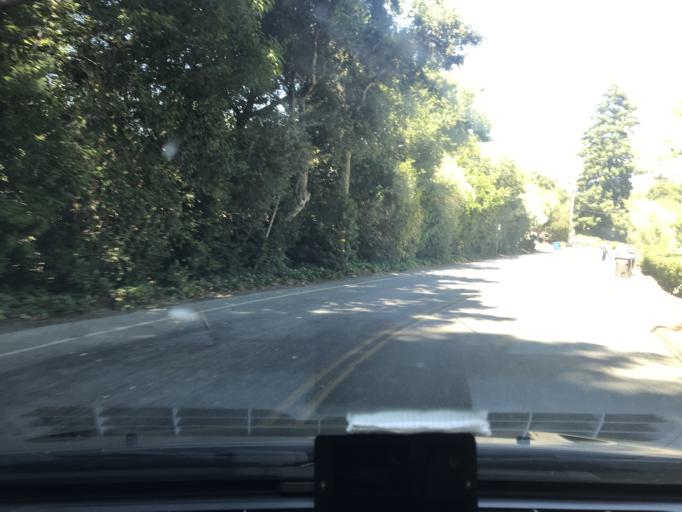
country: US
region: California
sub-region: Santa Clara County
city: Monte Sereno
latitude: 37.2301
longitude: -121.9954
